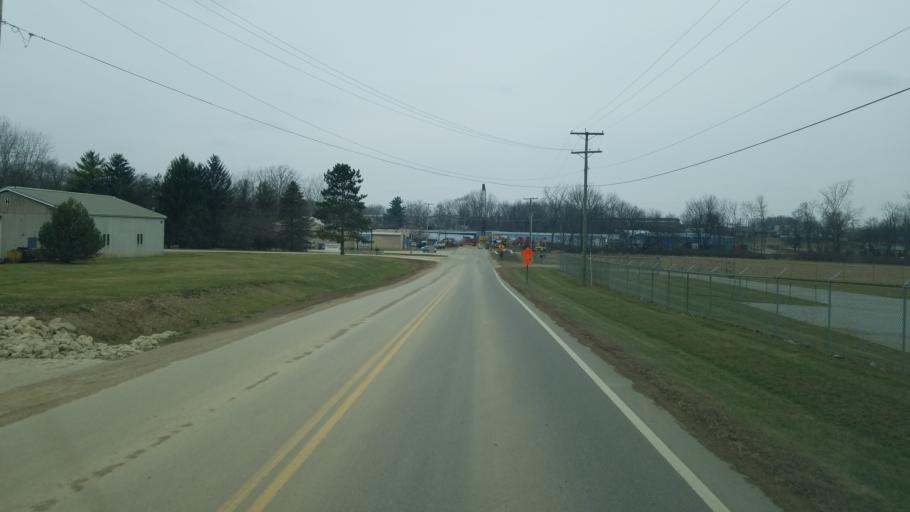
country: US
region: Ohio
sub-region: Knox County
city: Mount Vernon
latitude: 40.3768
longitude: -82.4946
